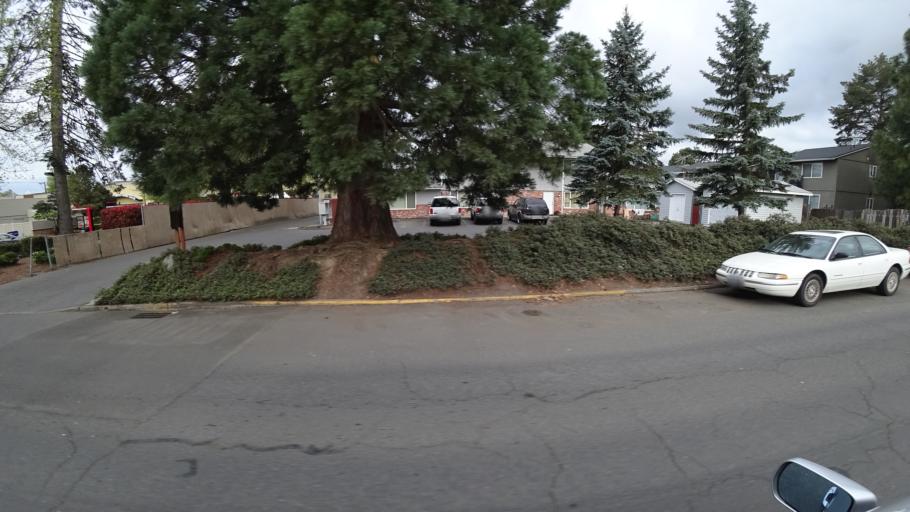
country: US
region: Oregon
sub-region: Washington County
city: Hillsboro
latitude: 45.5316
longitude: -122.9608
